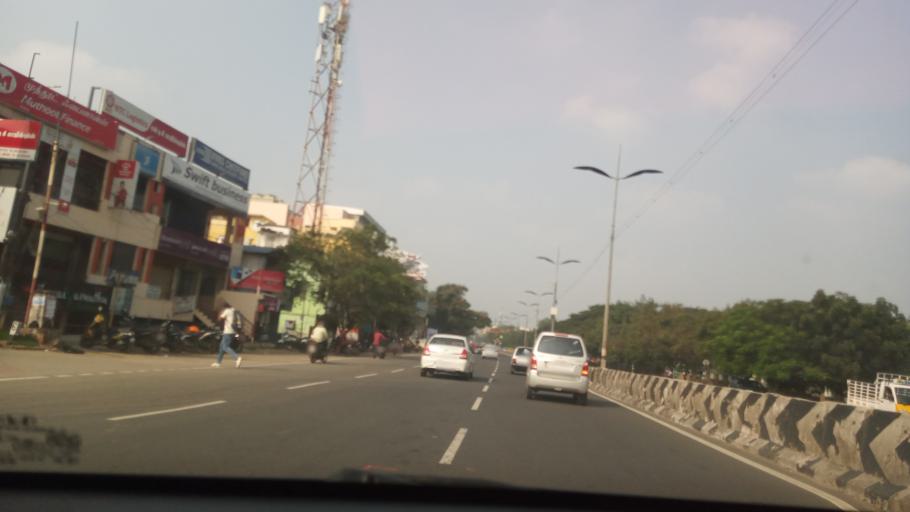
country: IN
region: Tamil Nadu
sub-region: Coimbatore
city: Singanallur
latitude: 11.0253
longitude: 77.0122
